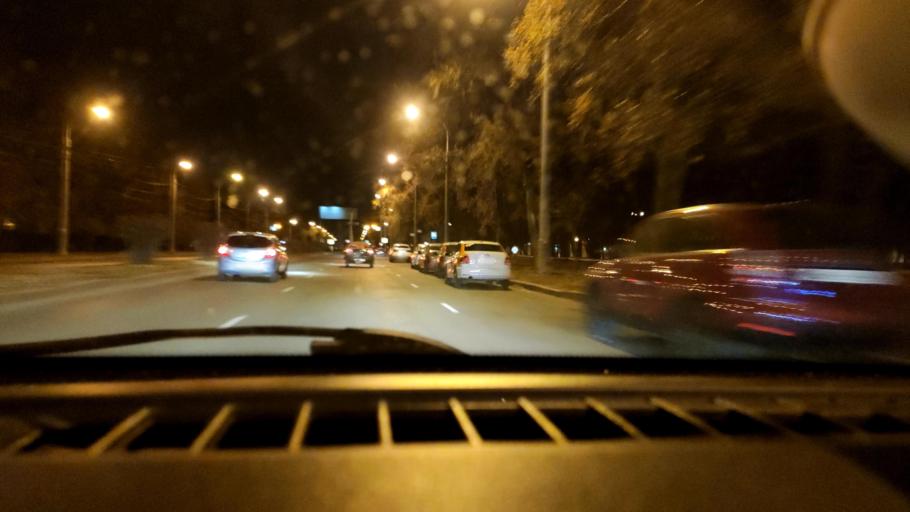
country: RU
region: Samara
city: Samara
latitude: 53.2306
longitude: 50.2047
